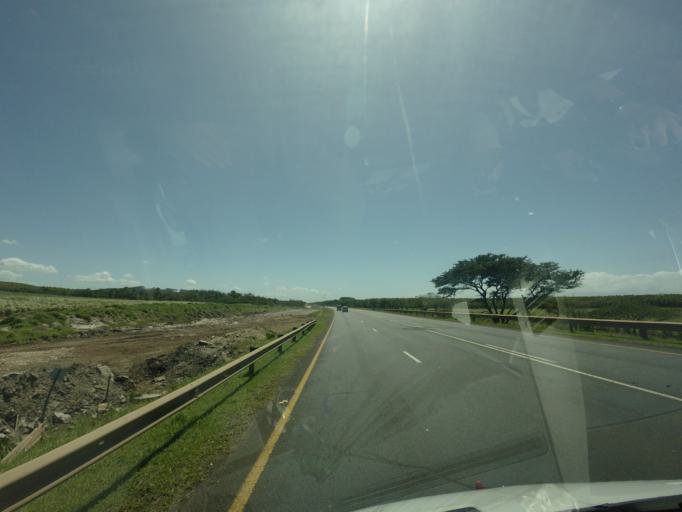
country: ZA
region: KwaZulu-Natal
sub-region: uThungulu District Municipality
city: eSikhawini
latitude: -28.9268
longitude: 31.7935
